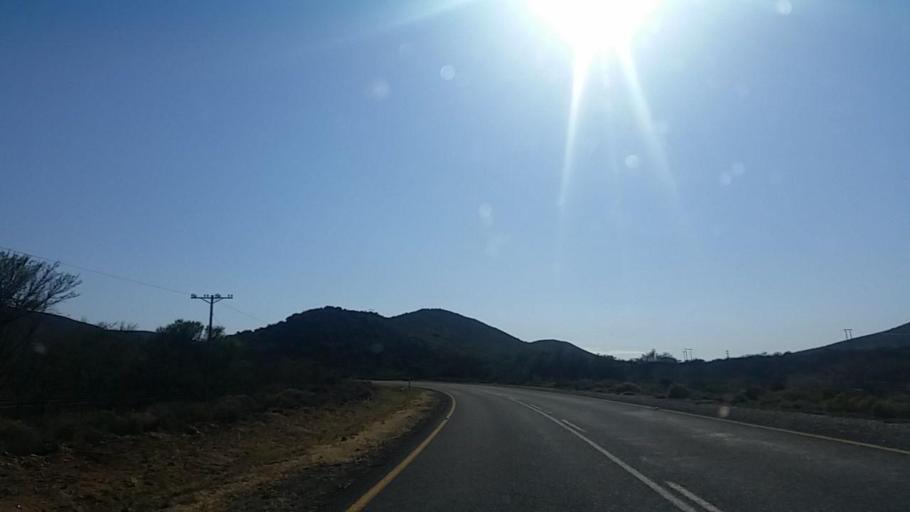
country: ZA
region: Eastern Cape
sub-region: Cacadu District Municipality
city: Willowmore
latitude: -33.4085
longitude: 23.3413
